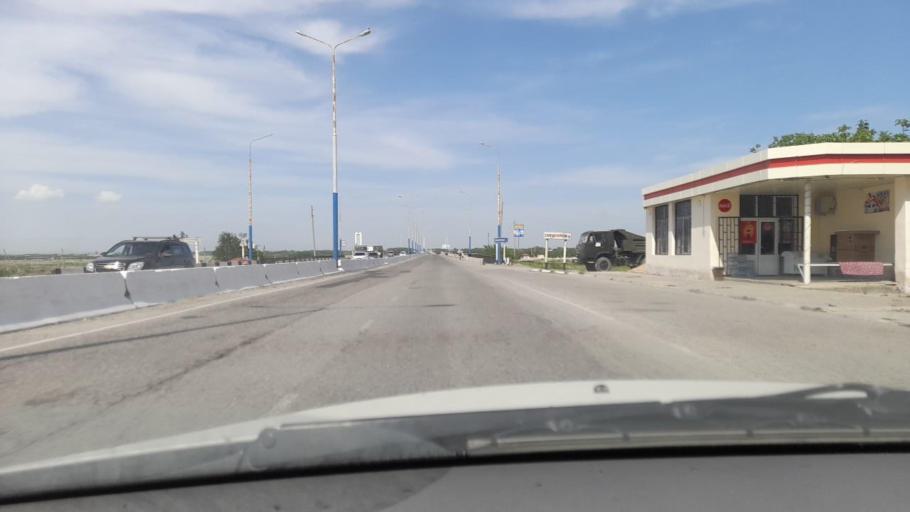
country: UZ
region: Samarqand
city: Kattaqo'rg'on
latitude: 39.9245
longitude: 66.3572
